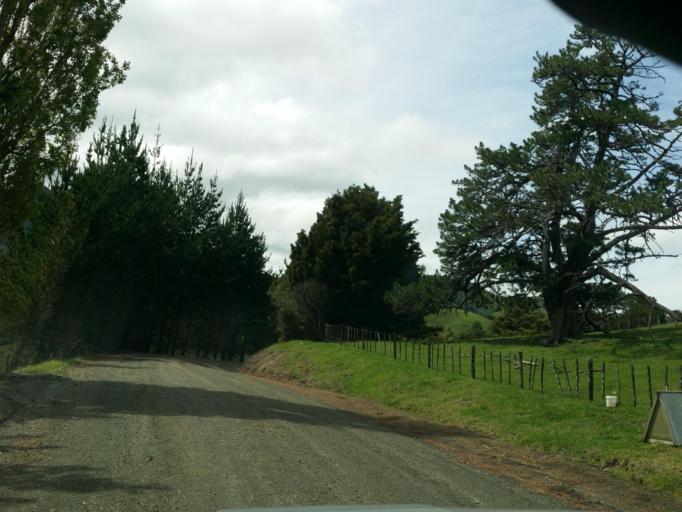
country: NZ
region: Northland
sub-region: Whangarei
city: Maungatapere
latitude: -35.8831
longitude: 174.0733
